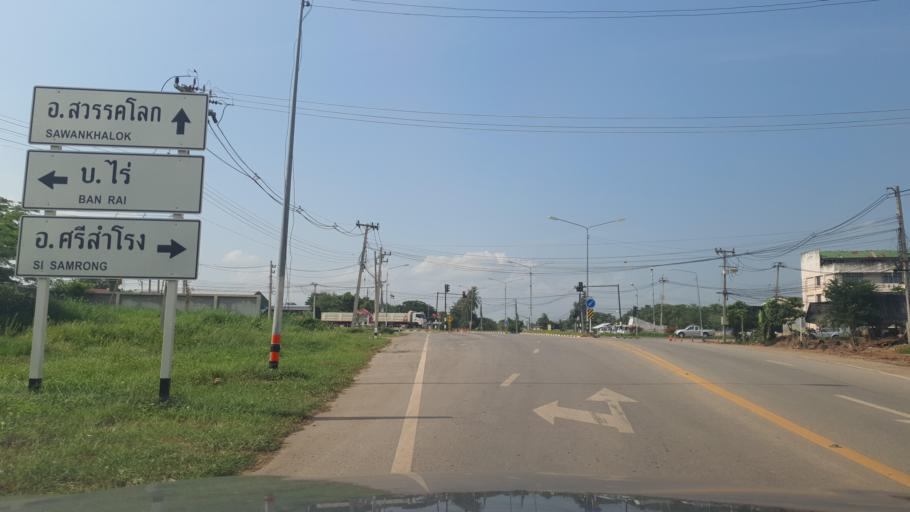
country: TH
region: Sukhothai
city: Si Samrong
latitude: 17.1744
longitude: 99.8515
